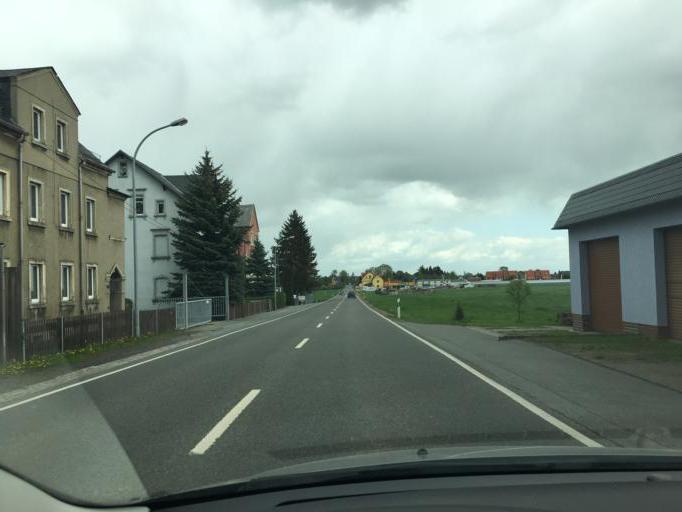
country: DE
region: Saxony
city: Limbach-Oberfrohna
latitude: 50.8387
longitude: 12.7660
